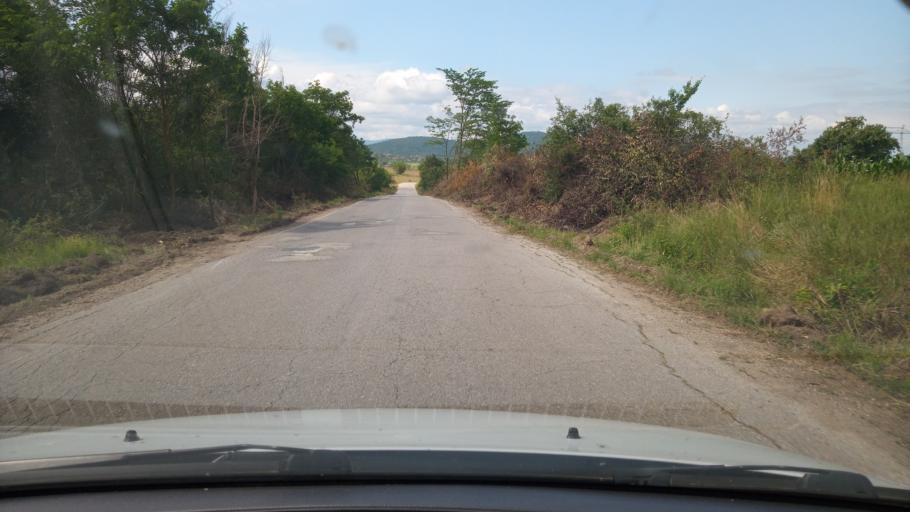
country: BG
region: Lovech
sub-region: Obshtina Lukovit
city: Lukovit
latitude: 43.1859
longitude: 24.0873
